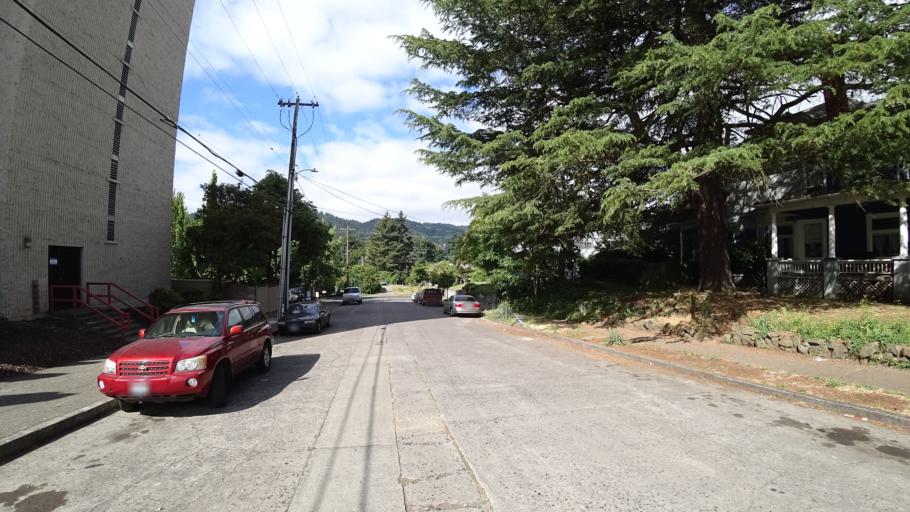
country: US
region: Oregon
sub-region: Washington County
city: West Haven
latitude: 45.5909
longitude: -122.7582
